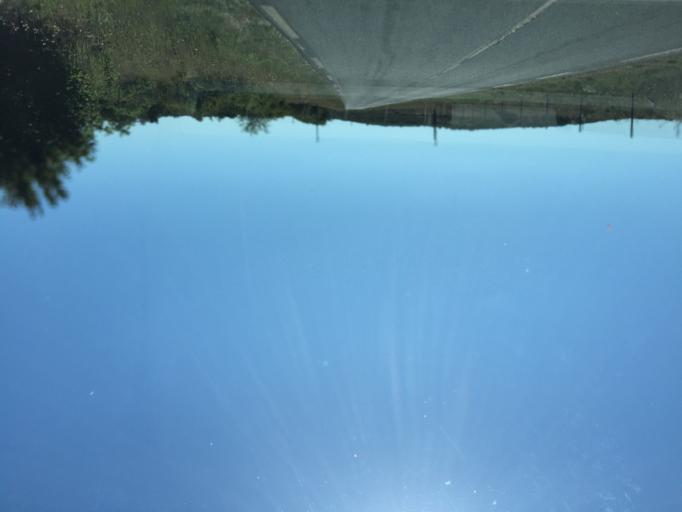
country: FR
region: Midi-Pyrenees
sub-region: Departement de l'Aveyron
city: La Cavalerie
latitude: 43.9190
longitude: 3.2496
